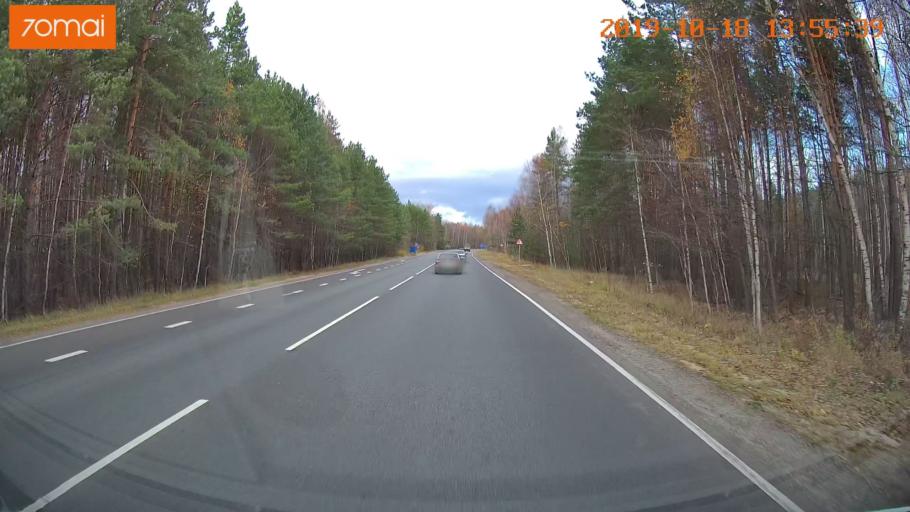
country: RU
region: Rjazan
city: Spas-Klepiki
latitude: 55.0547
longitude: 40.0243
